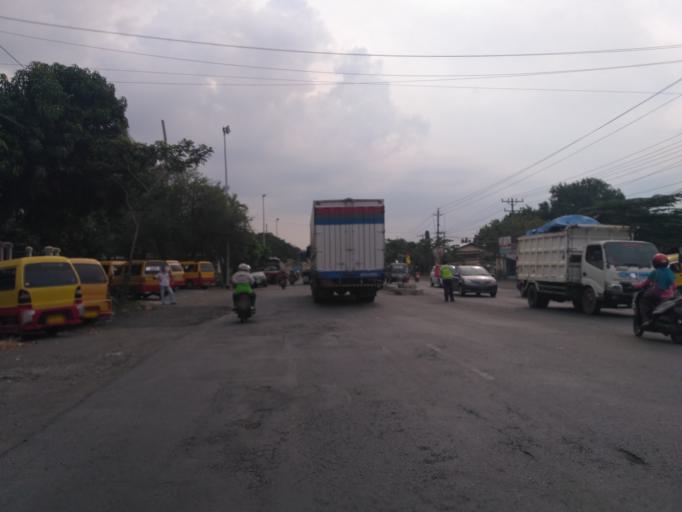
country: ID
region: Central Java
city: Semarang
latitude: -6.9760
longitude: 110.3229
